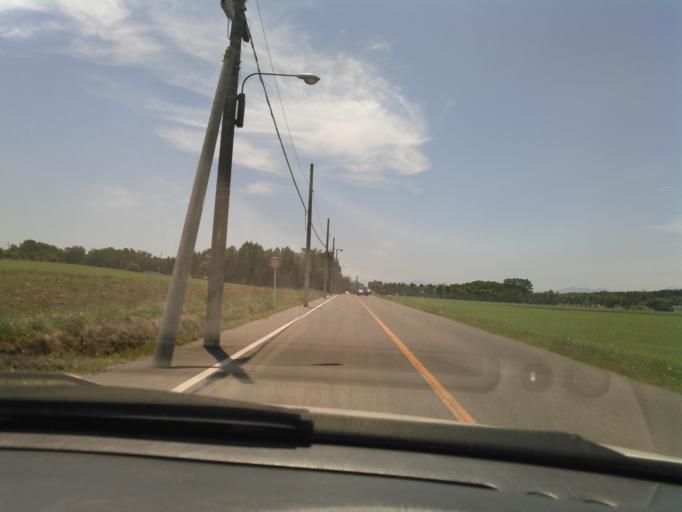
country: JP
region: Hokkaido
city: Ebetsu
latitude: 43.0808
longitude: 141.5183
